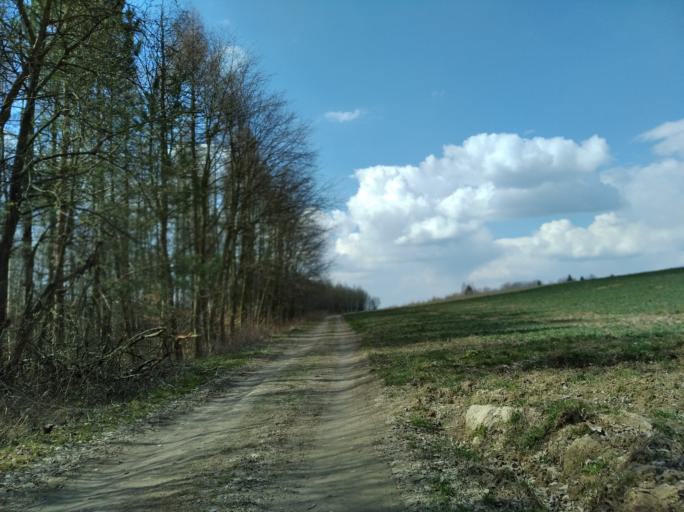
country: PL
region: Subcarpathian Voivodeship
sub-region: Powiat strzyzowski
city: Strzyzow
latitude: 49.9270
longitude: 21.7284
